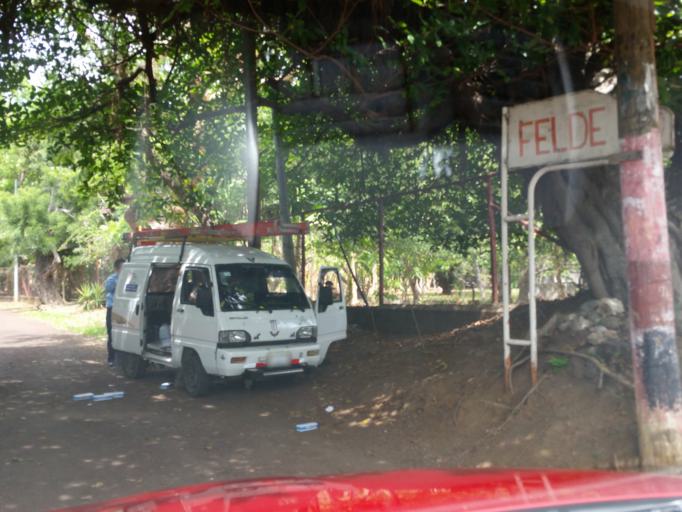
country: NI
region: Managua
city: Ciudad Sandino
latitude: 12.0905
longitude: -86.3239
